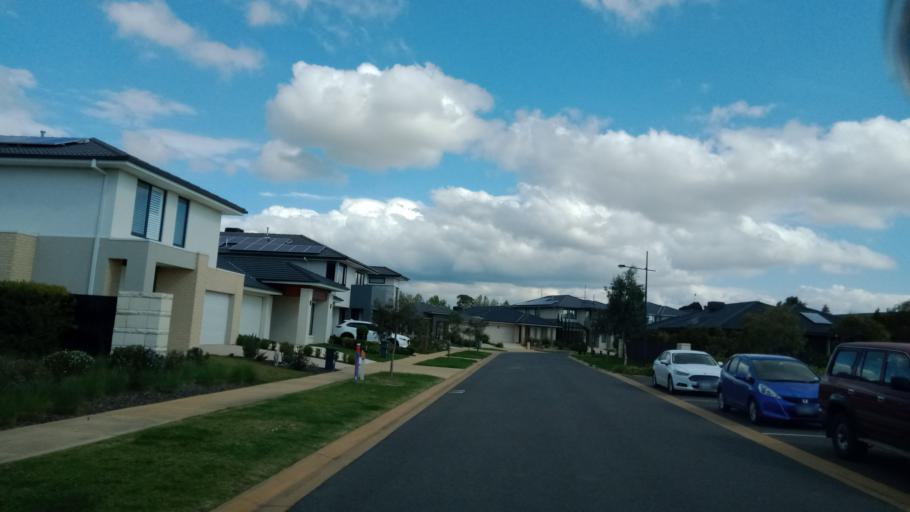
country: AU
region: Victoria
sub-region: Frankston
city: Sandhurst
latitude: -38.0794
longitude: 145.2094
